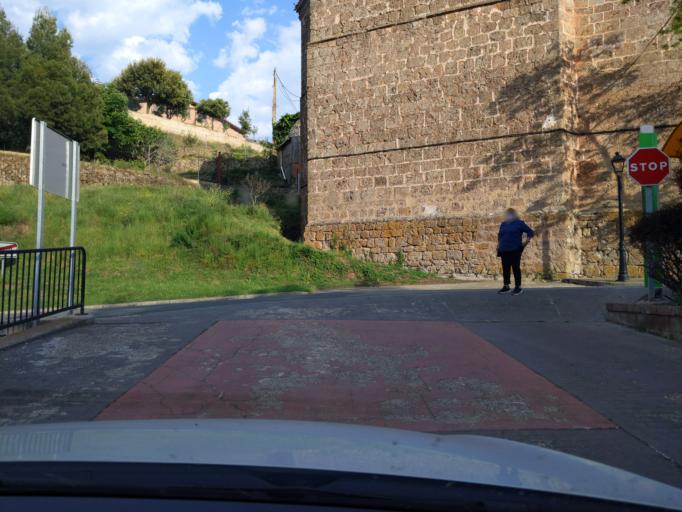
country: ES
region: La Rioja
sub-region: Provincia de La Rioja
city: Clavijo
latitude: 42.3498
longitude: -2.4261
